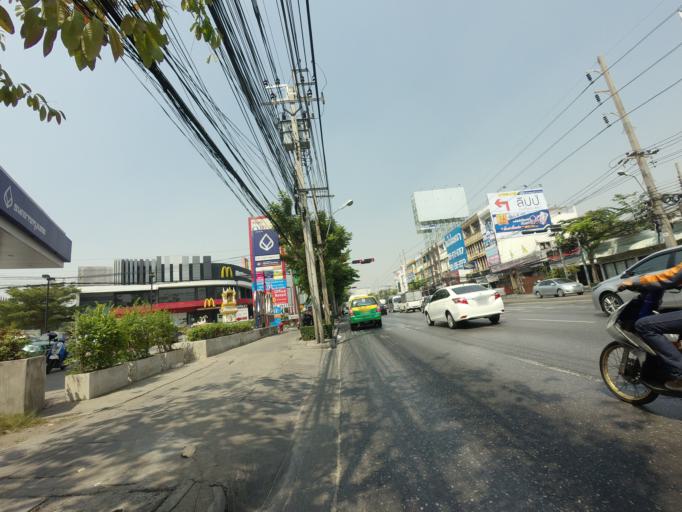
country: TH
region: Bangkok
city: Wang Thonglang
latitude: 13.7794
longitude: 100.6211
